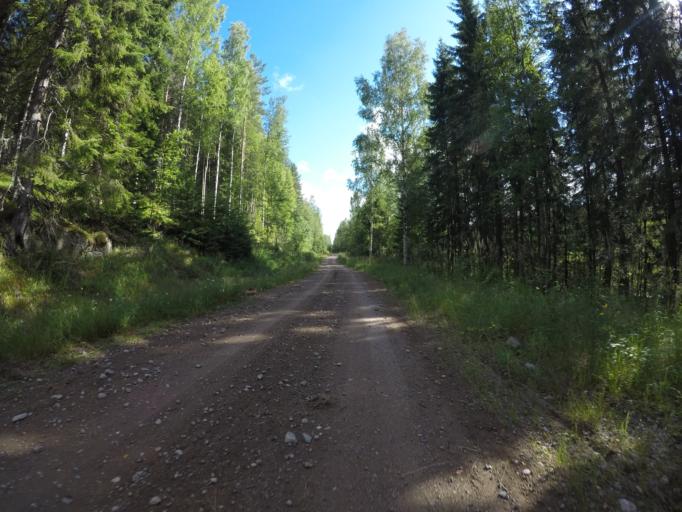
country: SE
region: OErebro
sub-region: Hallefors Kommun
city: Haellefors
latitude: 59.9977
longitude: 14.6052
